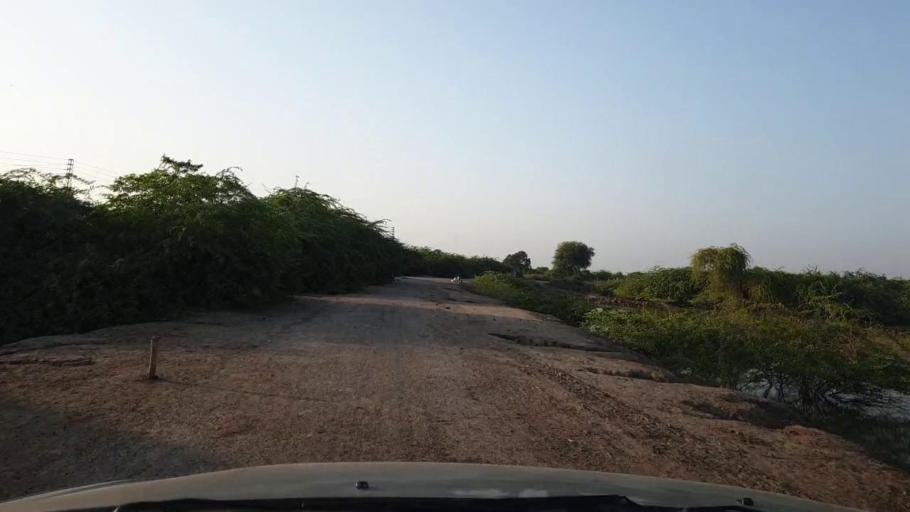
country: PK
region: Sindh
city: Tando Ghulam Ali
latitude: 25.1071
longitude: 68.9492
